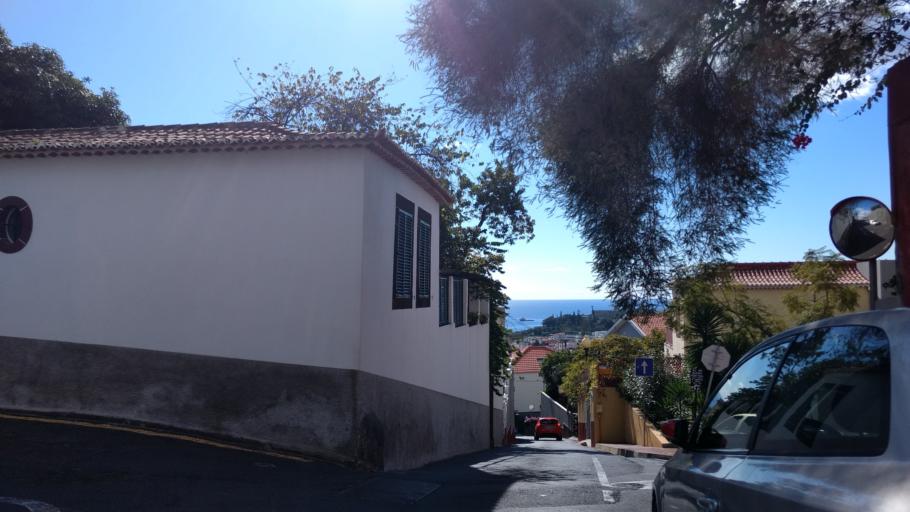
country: PT
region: Madeira
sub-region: Funchal
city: Nossa Senhora do Monte
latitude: 32.6560
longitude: -16.9080
